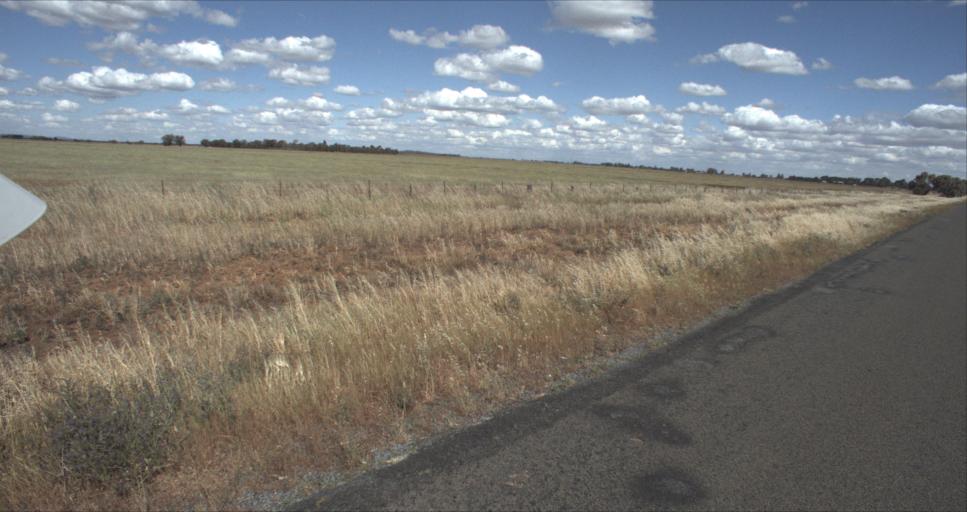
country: AU
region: New South Wales
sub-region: Leeton
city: Leeton
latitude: -34.4659
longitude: 146.2518
